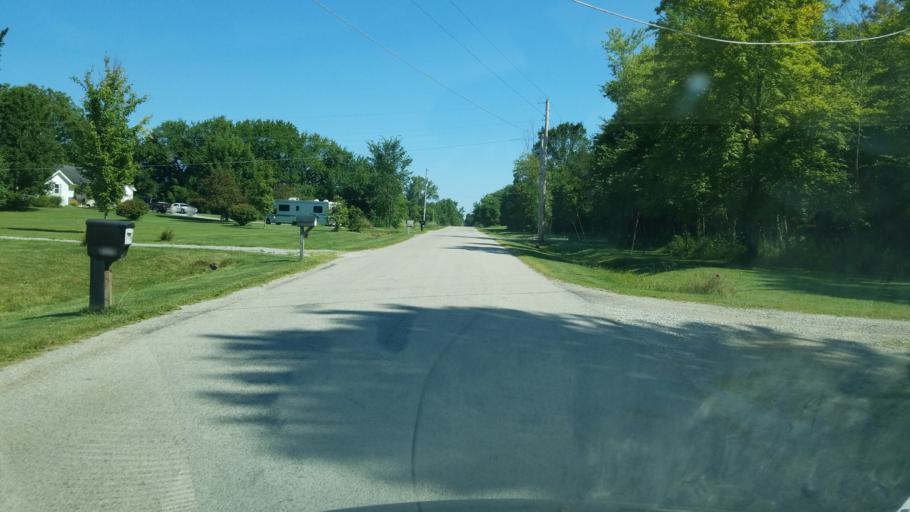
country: US
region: Ohio
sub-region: Knox County
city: Centerburg
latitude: 40.3720
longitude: -82.7627
